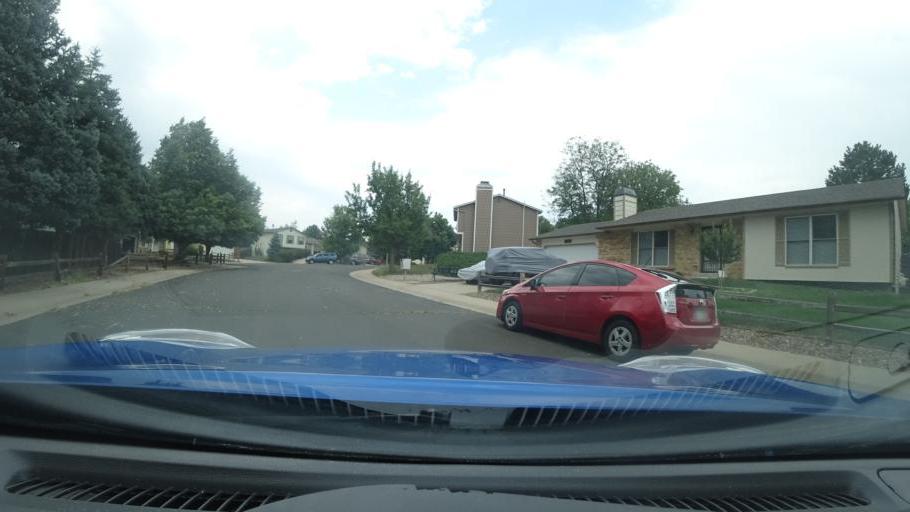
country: US
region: Colorado
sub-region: Adams County
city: Aurora
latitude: 39.6882
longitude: -104.7613
